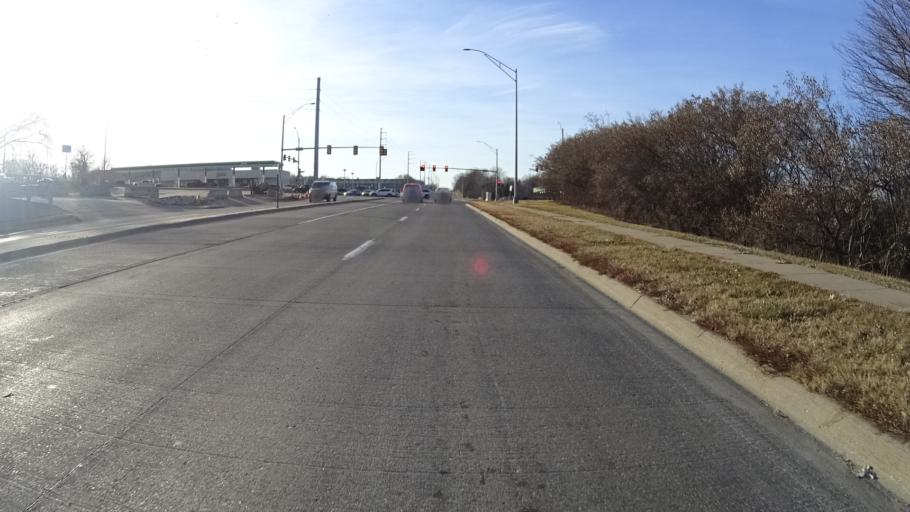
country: US
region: Nebraska
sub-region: Sarpy County
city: La Vista
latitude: 41.1908
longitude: -96.0225
